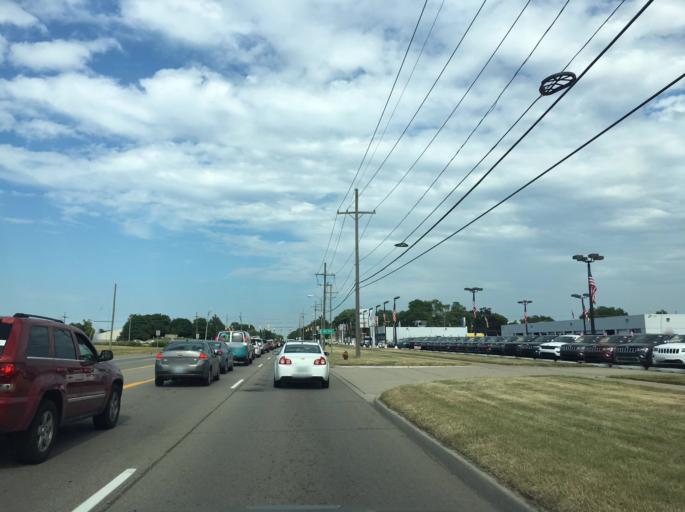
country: US
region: Michigan
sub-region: Macomb County
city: Sterling Heights
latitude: 42.5365
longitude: -83.0320
